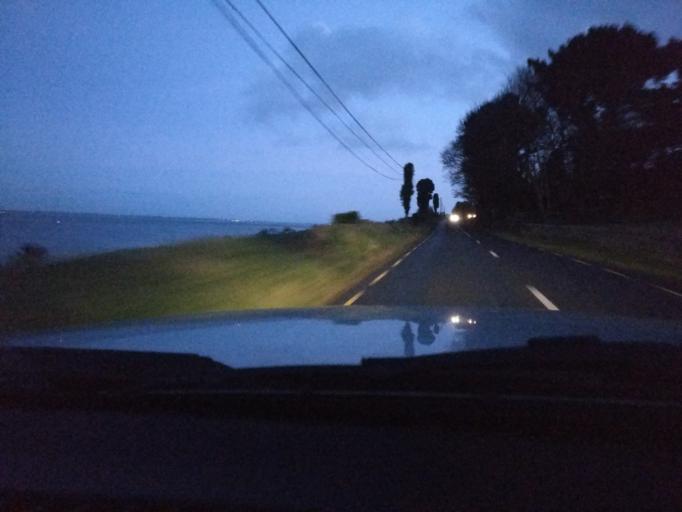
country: IE
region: Leinster
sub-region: Lu
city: Carlingford
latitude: 54.0617
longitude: -6.2079
